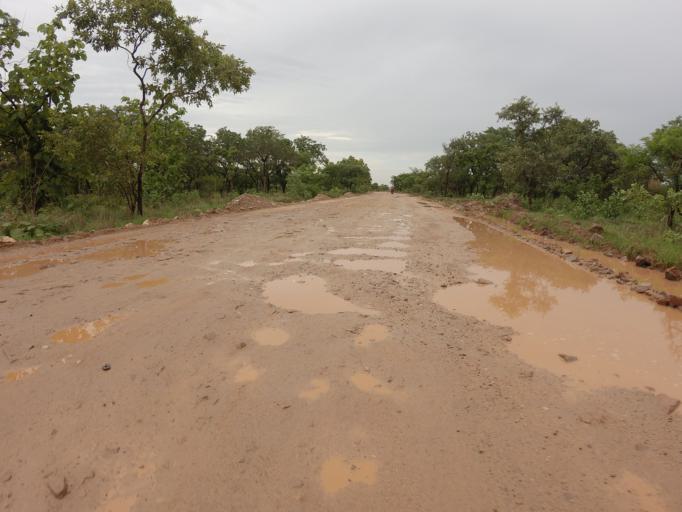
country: GH
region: Upper East
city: Bolgatanga
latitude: 10.8783
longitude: -0.6345
